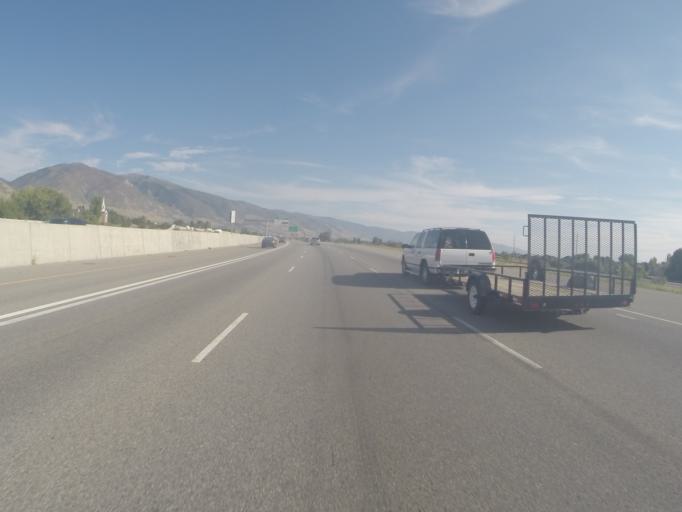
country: US
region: Utah
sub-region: Davis County
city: Kaysville
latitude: 41.0119
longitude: -111.9383
